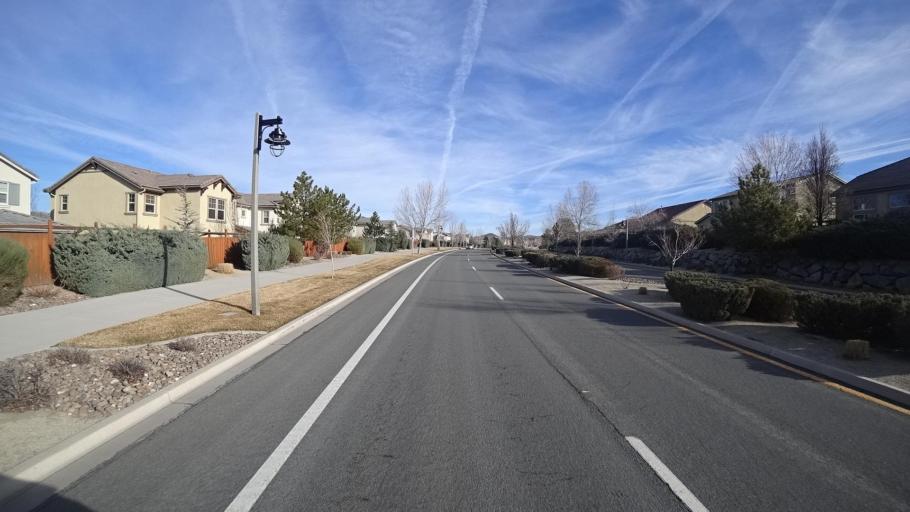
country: US
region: Nevada
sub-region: Washoe County
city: Spanish Springs
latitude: 39.6154
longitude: -119.6707
